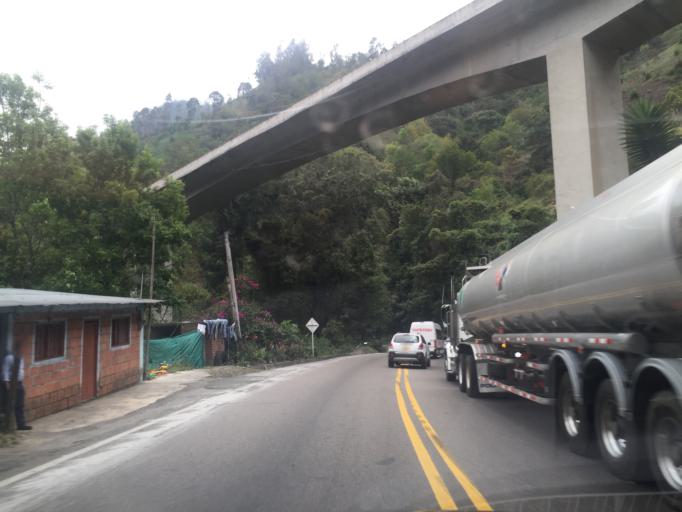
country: CO
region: Tolima
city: Cajamarca
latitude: 4.4337
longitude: -75.4590
